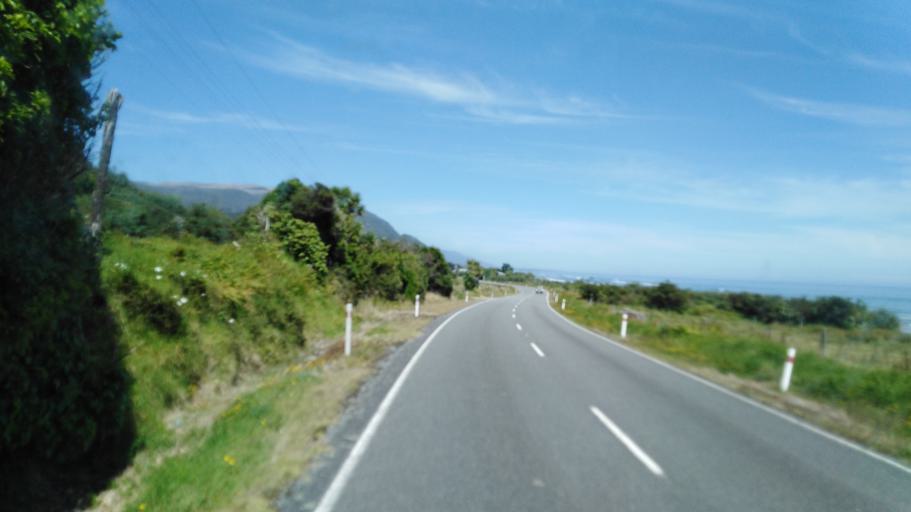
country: NZ
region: West Coast
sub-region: Buller District
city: Westport
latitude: -41.5953
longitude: 171.8875
